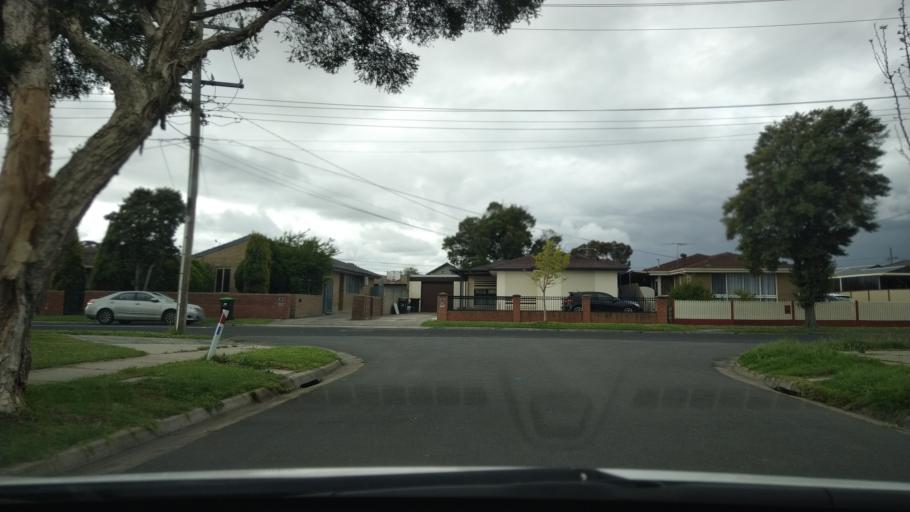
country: AU
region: Victoria
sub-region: Greater Dandenong
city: Springvale South
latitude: -37.9778
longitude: 145.1512
